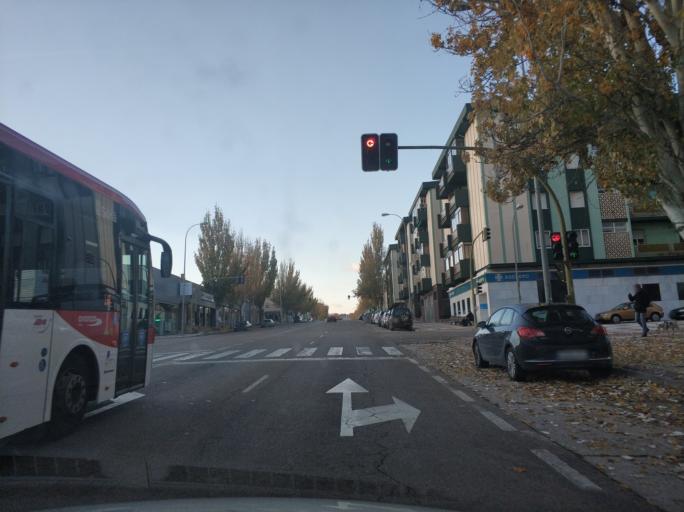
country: ES
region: Castille and Leon
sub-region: Provincia de Soria
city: Soria
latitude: 41.7587
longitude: -2.4745
